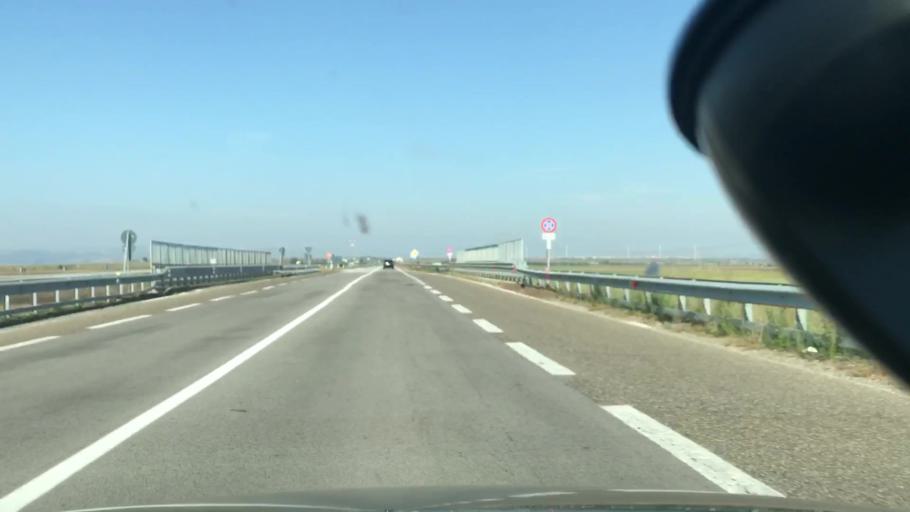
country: IT
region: Basilicate
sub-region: Provincia di Potenza
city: Venosa
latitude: 40.9938
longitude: 15.8879
